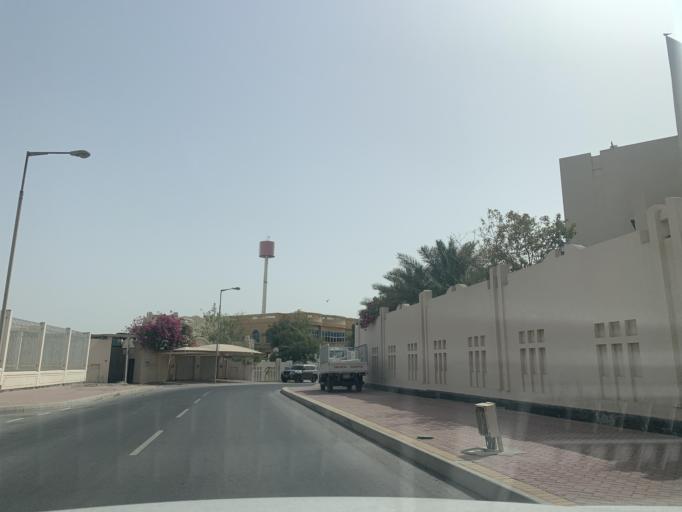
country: BH
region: Central Governorate
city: Madinat Hamad
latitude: 26.1441
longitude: 50.5131
